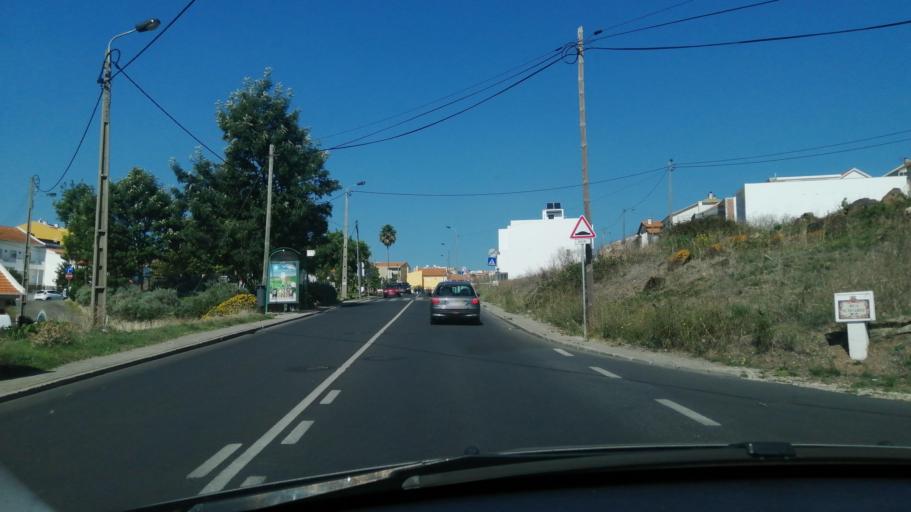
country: PT
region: Lisbon
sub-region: Odivelas
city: Canecas
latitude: 38.7975
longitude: -9.2264
